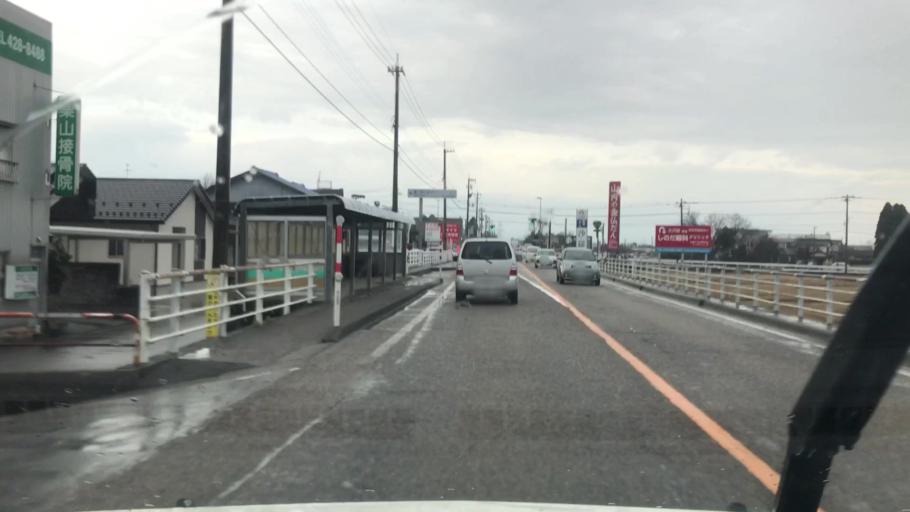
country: JP
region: Toyama
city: Toyama-shi
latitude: 36.6196
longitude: 137.2054
